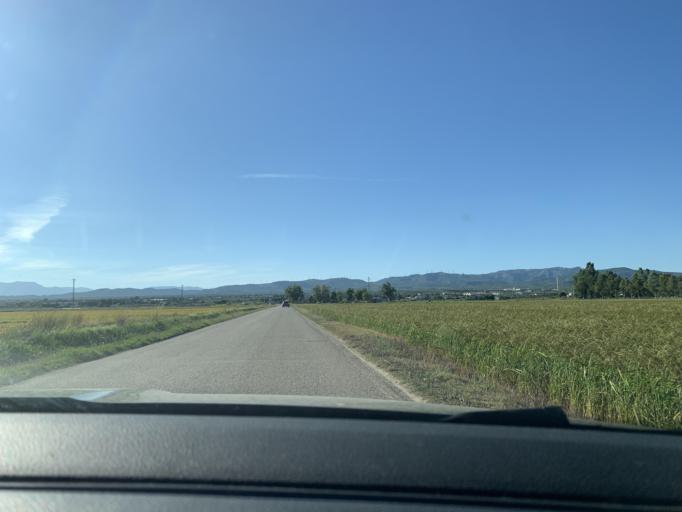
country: ES
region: Catalonia
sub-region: Provincia de Tarragona
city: Camarles
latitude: 40.7744
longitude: 0.6928
